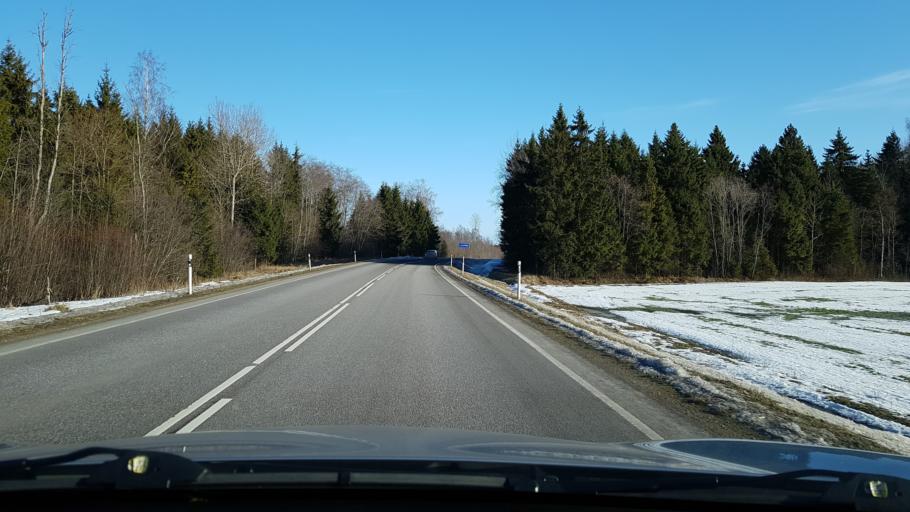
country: EE
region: Viljandimaa
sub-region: Vohma linn
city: Vohma
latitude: 58.6342
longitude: 25.7411
